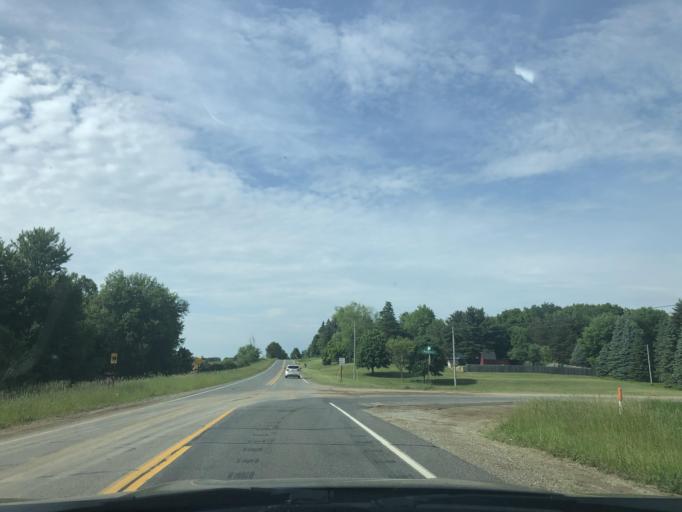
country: US
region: Michigan
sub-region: Clinton County
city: Bath
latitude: 42.8054
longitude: -84.4837
